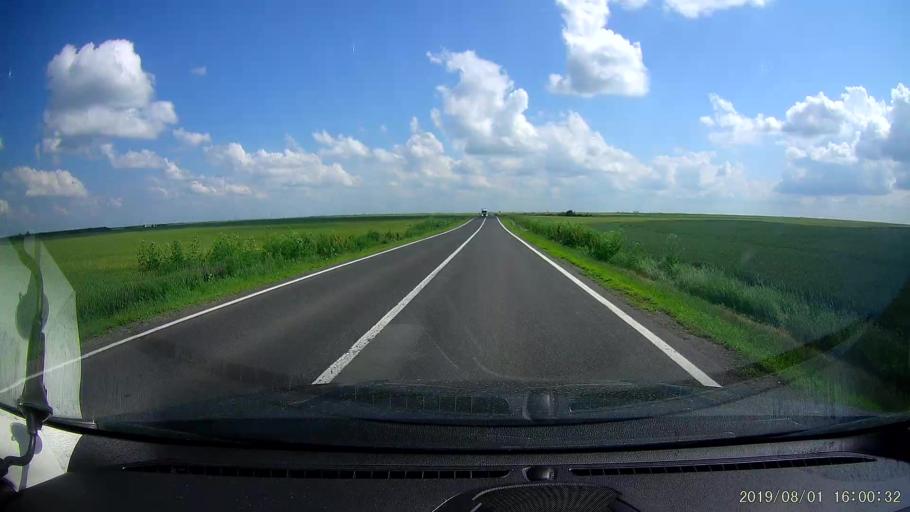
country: RO
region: Ialomita
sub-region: Comuna Ciulnita
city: Ciulnita
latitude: 44.5270
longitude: 27.3890
